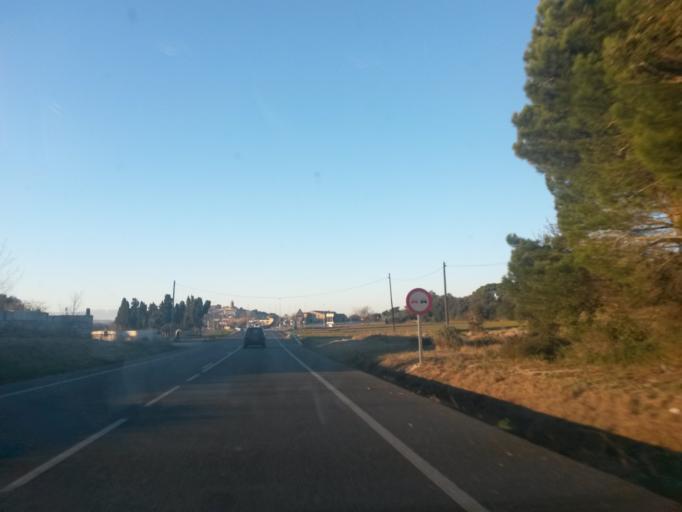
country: ES
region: Catalonia
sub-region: Provincia de Girona
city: Pals
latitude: 41.9631
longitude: 3.1518
